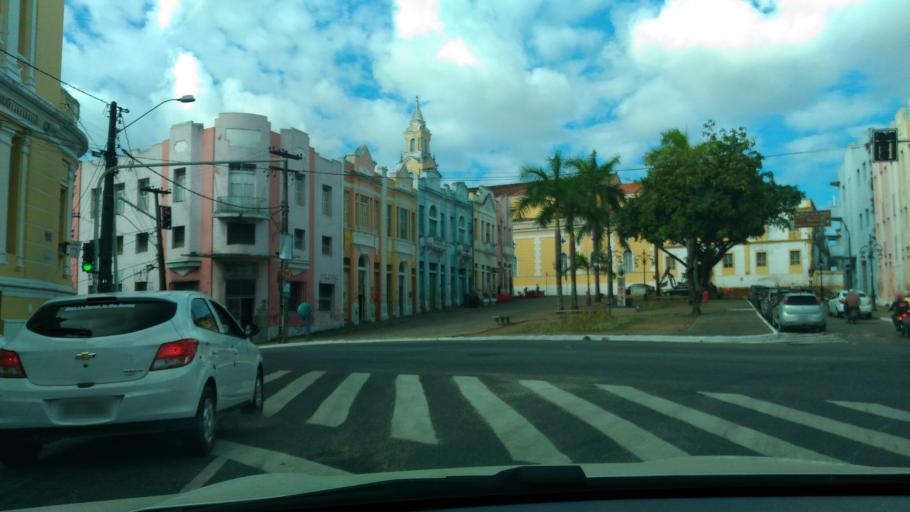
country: BR
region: Paraiba
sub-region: Joao Pessoa
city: Joao Pessoa
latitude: -7.1140
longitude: -34.8887
